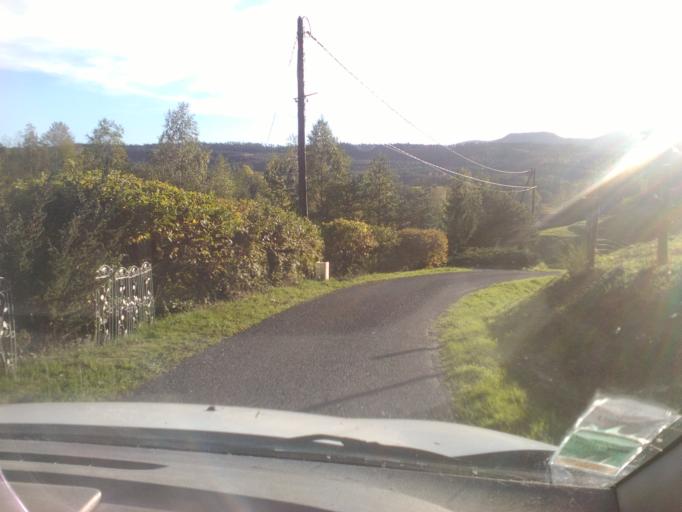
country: FR
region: Lorraine
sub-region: Departement des Vosges
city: Taintrux
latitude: 48.2537
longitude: 6.9167
